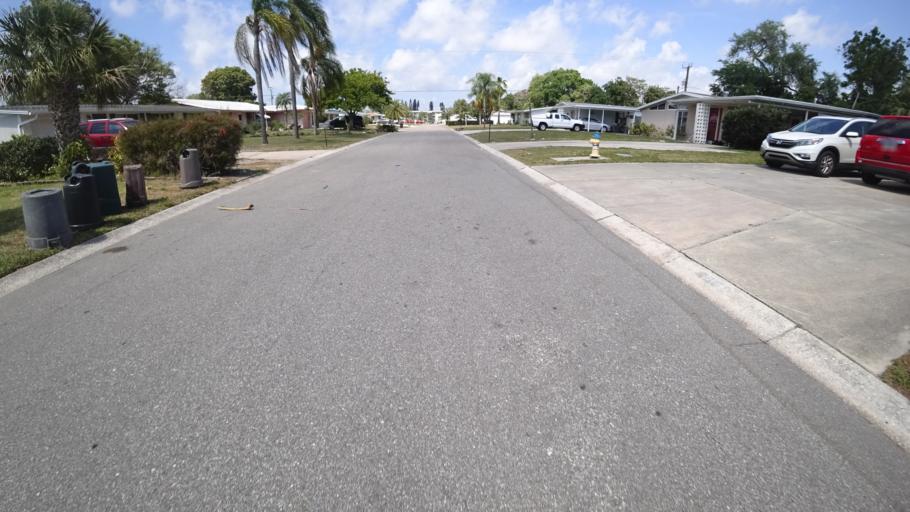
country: US
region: Florida
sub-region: Manatee County
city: Bayshore Gardens
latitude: 27.4323
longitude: -82.5821
